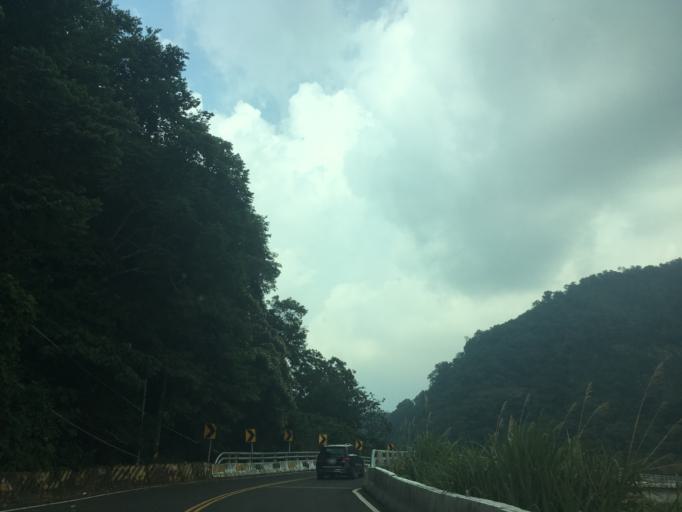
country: TW
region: Taiwan
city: Fengyuan
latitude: 24.2947
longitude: 120.9094
